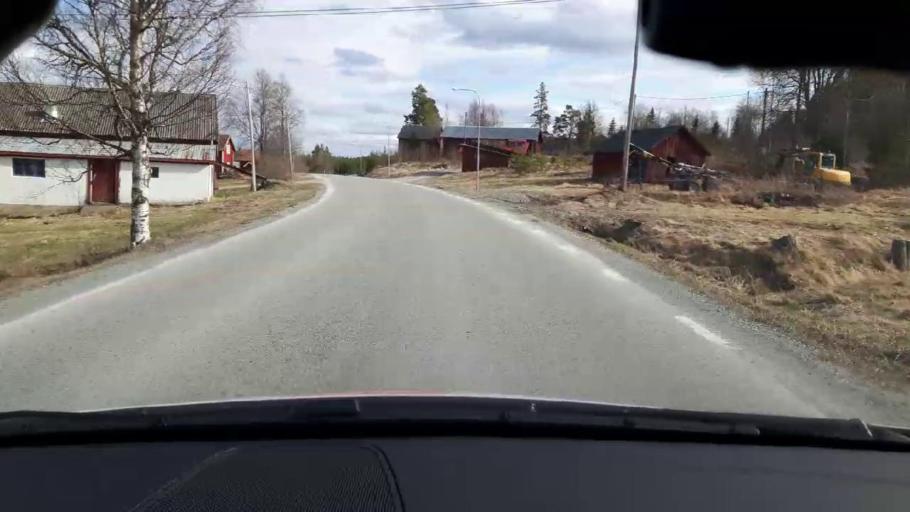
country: SE
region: Jaemtland
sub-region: Bergs Kommun
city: Hoverberg
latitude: 62.7627
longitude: 14.5583
